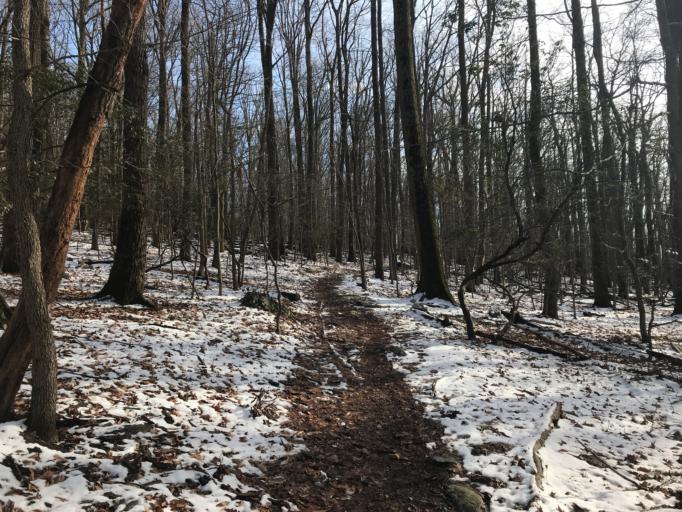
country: US
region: Maryland
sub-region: Frederick County
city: Braddock Heights
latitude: 39.4640
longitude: -77.4975
